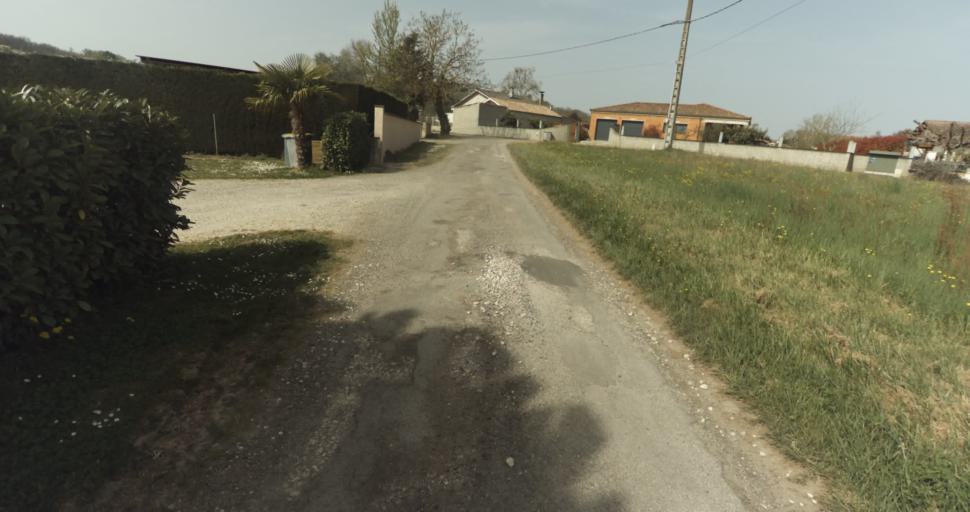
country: FR
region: Midi-Pyrenees
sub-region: Departement du Tarn-et-Garonne
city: Moissac
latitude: 44.1245
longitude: 1.1527
